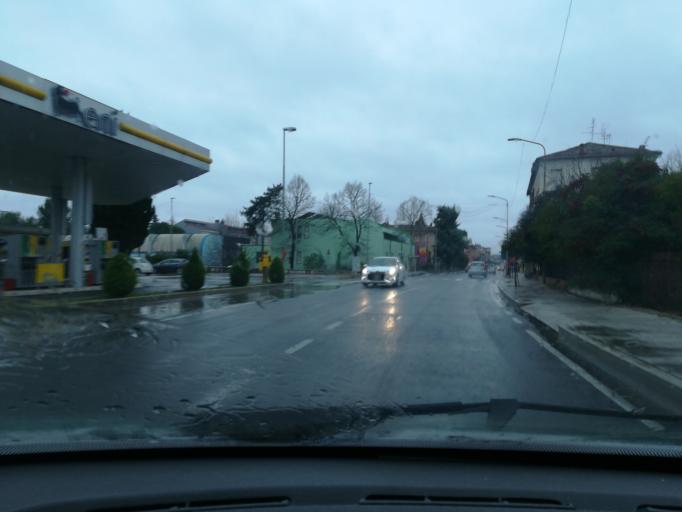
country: IT
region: The Marches
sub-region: Provincia di Macerata
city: Sforzacosta
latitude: 43.2586
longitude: 13.4214
